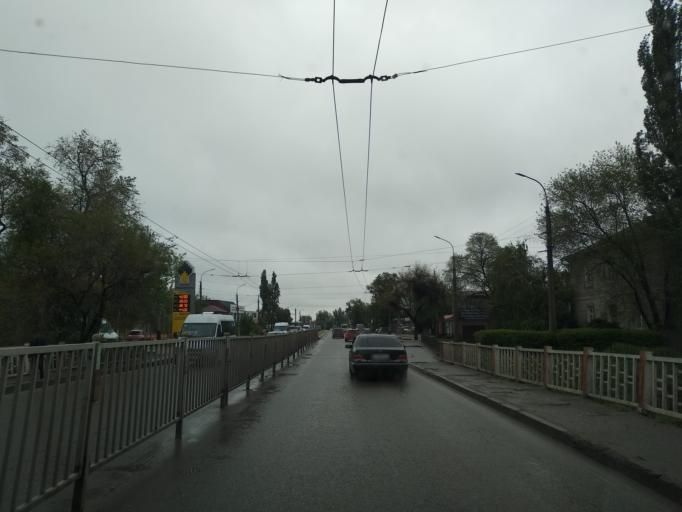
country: KG
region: Chuy
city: Bishkek
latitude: 42.8871
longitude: 74.6306
